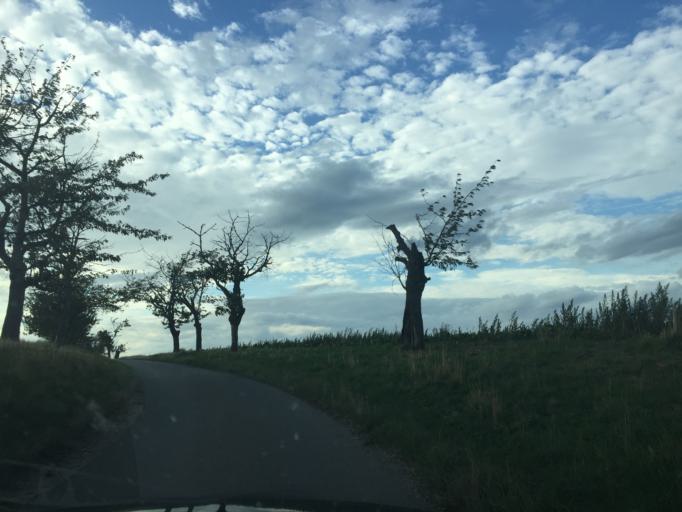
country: DE
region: Thuringia
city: Altkirchen
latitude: 50.9164
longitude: 12.3551
